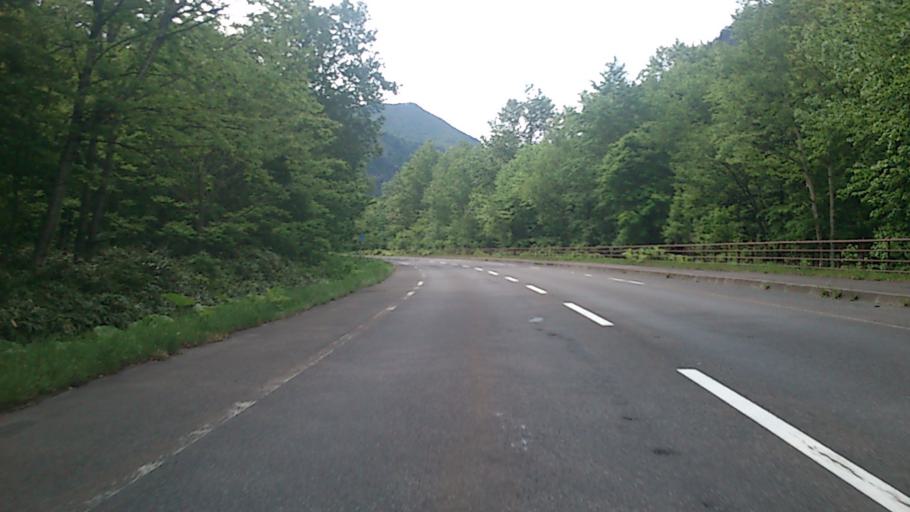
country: JP
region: Hokkaido
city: Kamikawa
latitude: 43.7587
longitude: 142.9216
